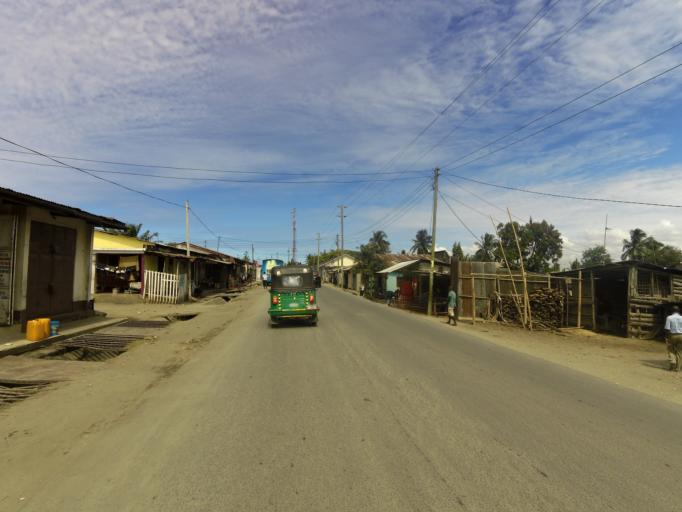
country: TZ
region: Dar es Salaam
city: Magomeni
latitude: -6.7871
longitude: 39.2403
